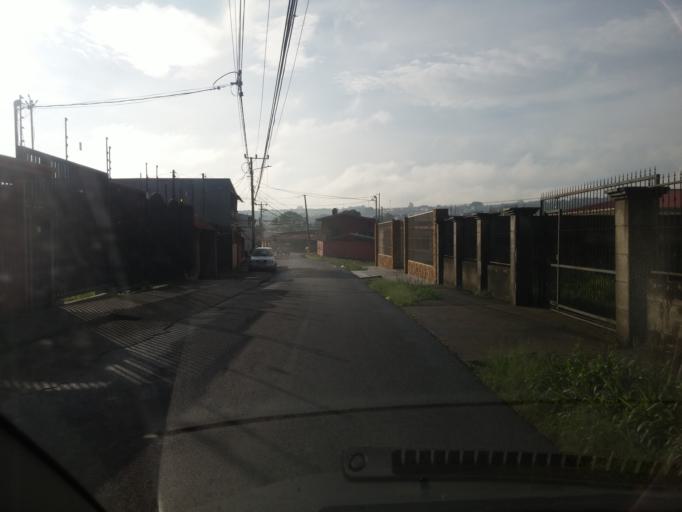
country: CR
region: Heredia
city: Llorente
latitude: 9.9971
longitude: -84.1546
